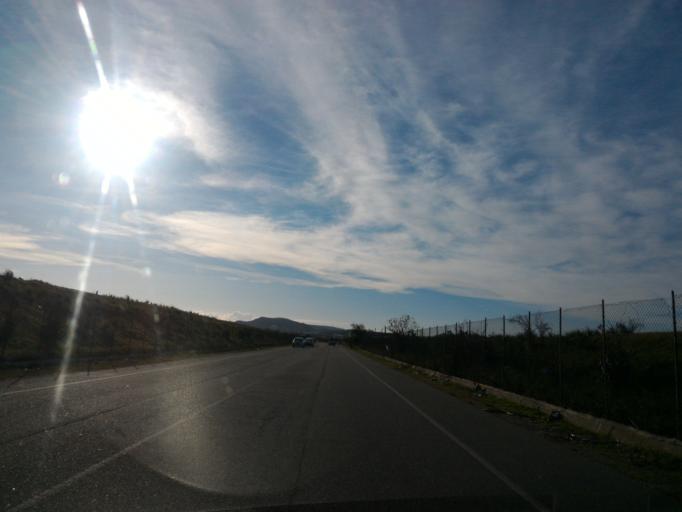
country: IT
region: Calabria
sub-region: Provincia di Crotone
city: Crotone
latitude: 39.1009
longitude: 17.1087
